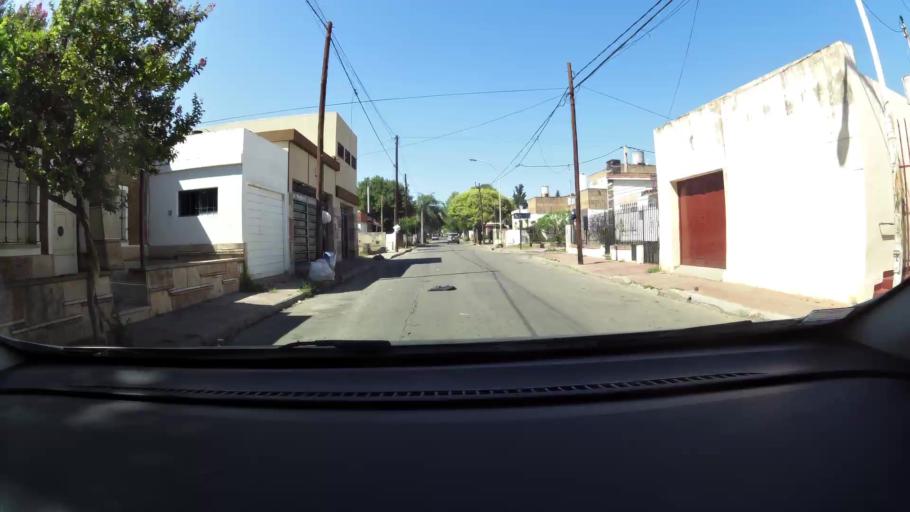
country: AR
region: Cordoba
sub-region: Departamento de Capital
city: Cordoba
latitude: -31.4155
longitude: -64.2174
